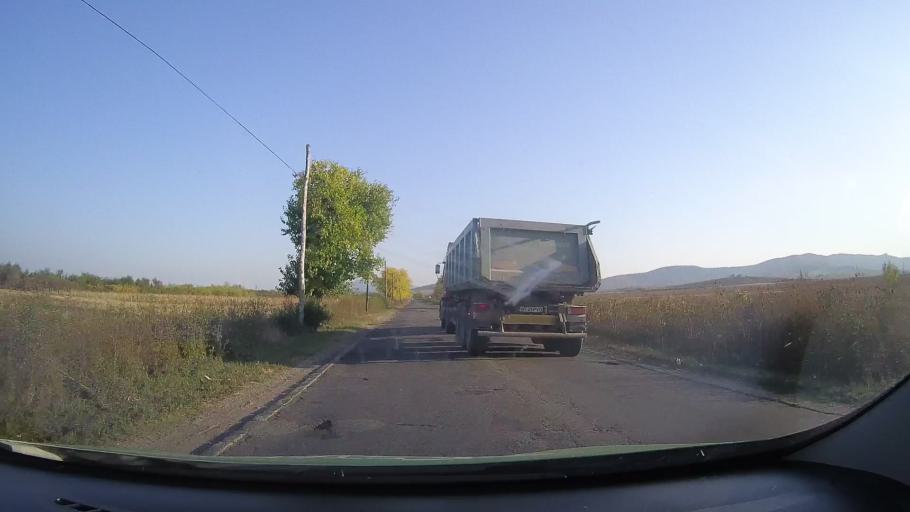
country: RO
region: Arad
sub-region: Comuna Pancota
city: Pancota
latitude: 46.3152
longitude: 21.7010
